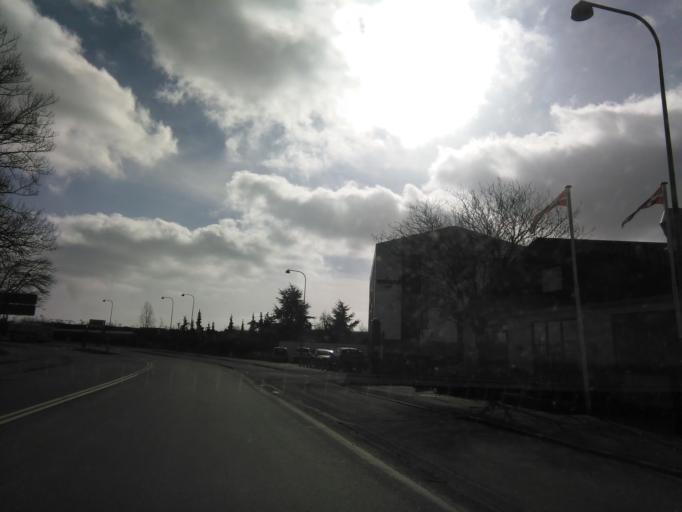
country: DK
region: Capital Region
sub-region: Dragor Kommune
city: Dragor
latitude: 55.6338
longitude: 12.6533
